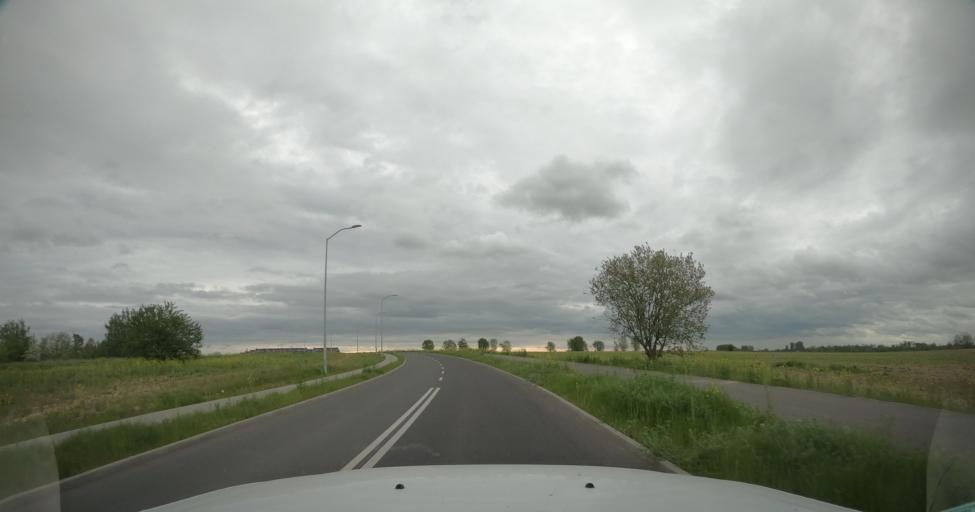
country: PL
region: West Pomeranian Voivodeship
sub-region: Powiat stargardzki
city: Stargard Szczecinski
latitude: 53.3095
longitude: 15.0289
